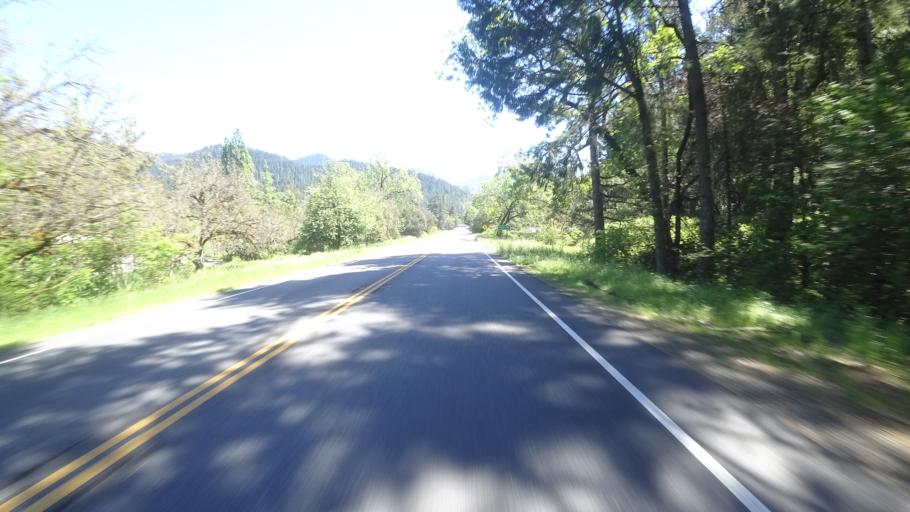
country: US
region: California
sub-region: Humboldt County
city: Willow Creek
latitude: 40.8717
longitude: -123.5276
